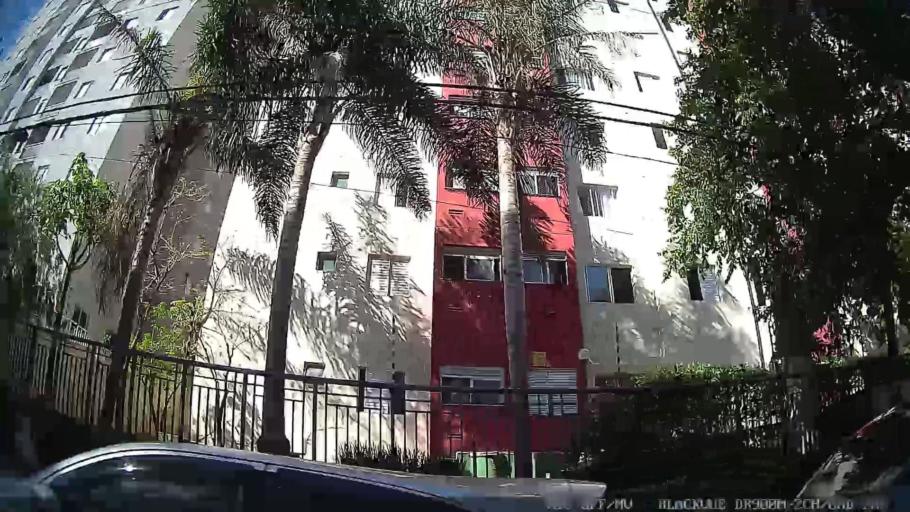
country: BR
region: Sao Paulo
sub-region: Guarulhos
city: Guarulhos
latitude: -23.5431
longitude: -46.5099
